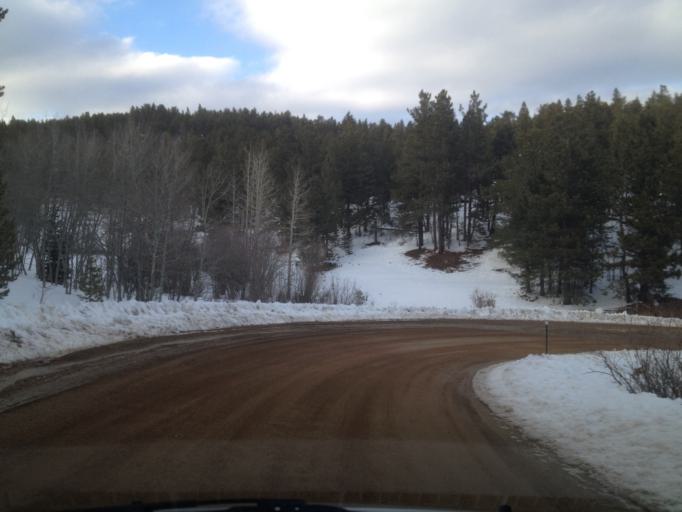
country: US
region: Colorado
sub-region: Boulder County
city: Nederland
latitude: 40.1240
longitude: -105.4560
